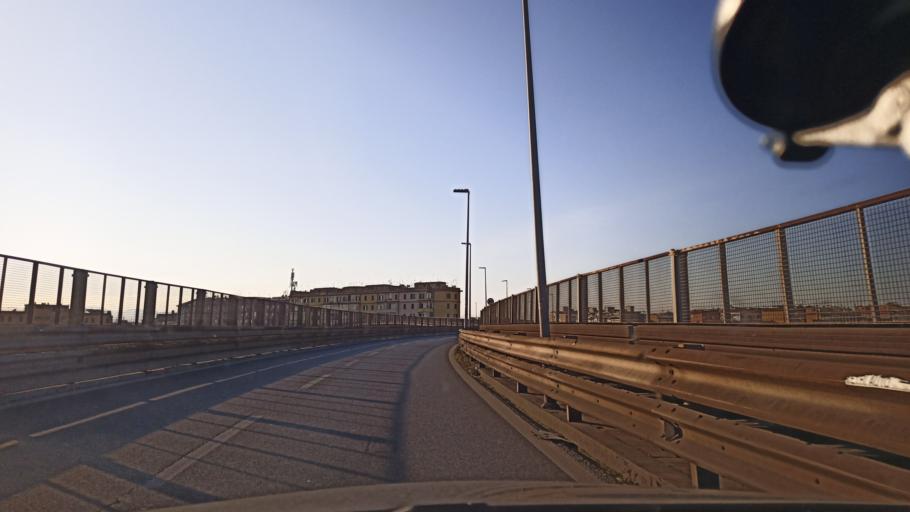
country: IT
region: Latium
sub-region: Citta metropolitana di Roma Capitale
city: Rome
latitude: 41.8929
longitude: 12.5198
